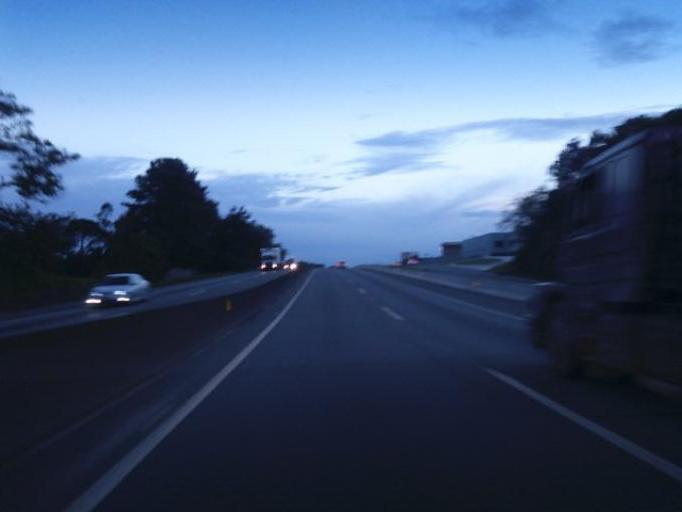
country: BR
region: Santa Catarina
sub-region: Joinville
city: Joinville
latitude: -26.3339
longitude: -48.8607
